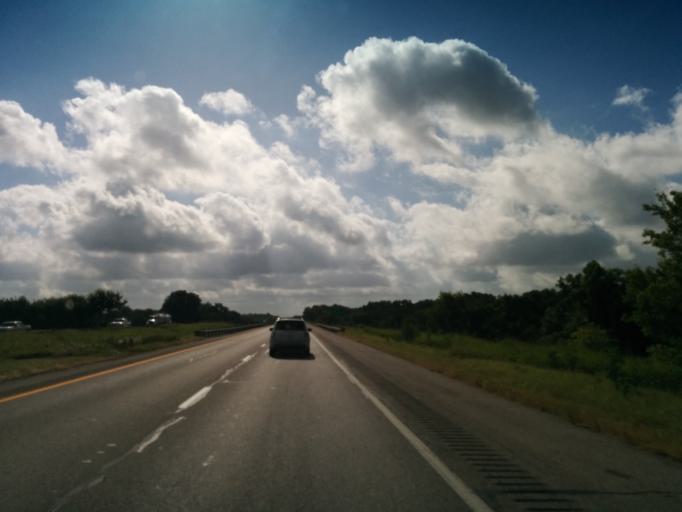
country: US
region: Texas
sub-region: Caldwell County
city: Luling
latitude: 29.6495
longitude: -97.6379
